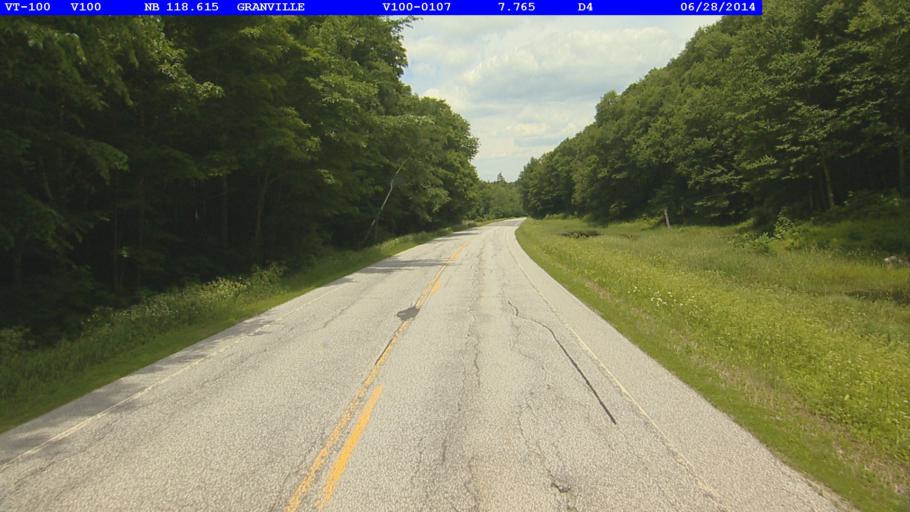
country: US
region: Vermont
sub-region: Orange County
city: Randolph
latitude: 44.0422
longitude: -72.8323
